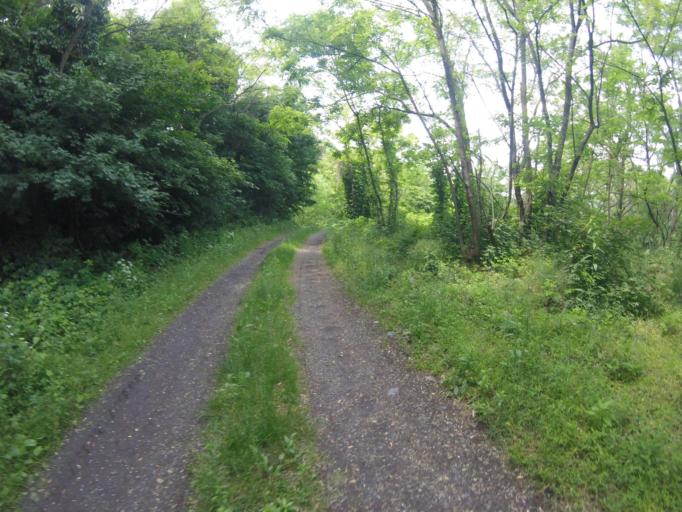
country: HU
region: Zala
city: Turje
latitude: 46.9144
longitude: 17.1801
